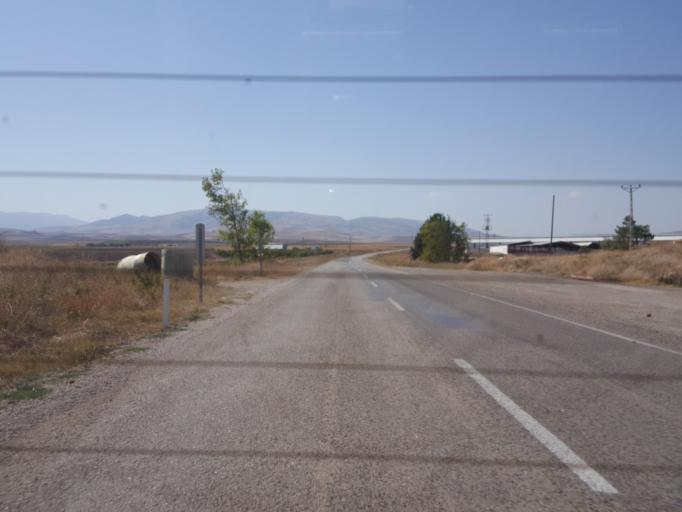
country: TR
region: Amasya
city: Dogantepe
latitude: 40.5794
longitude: 35.6337
